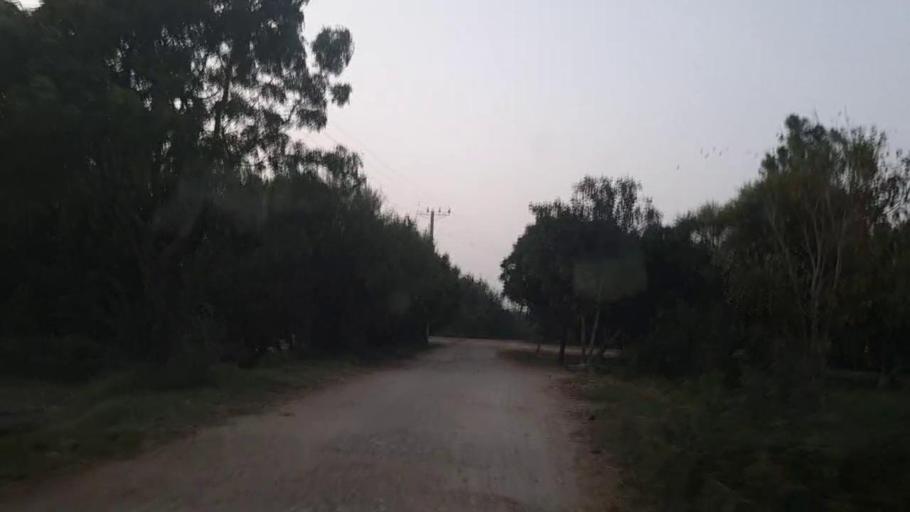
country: PK
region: Sindh
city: Mirpur Sakro
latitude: 24.5898
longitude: 67.7816
